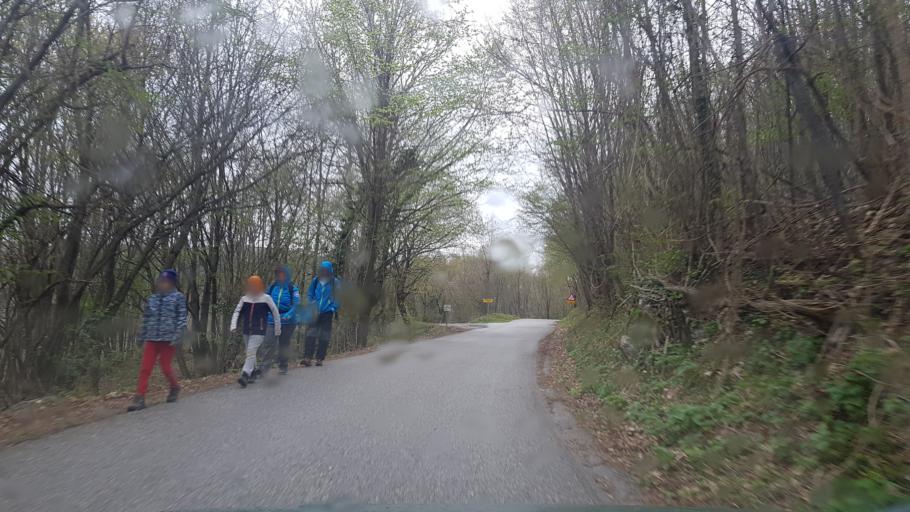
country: SI
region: Kanal
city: Deskle
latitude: 46.0513
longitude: 13.5660
